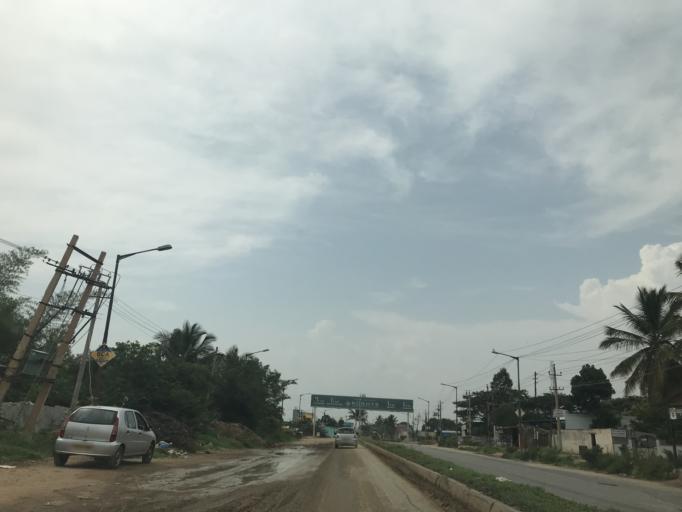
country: IN
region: Karnataka
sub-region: Bangalore Urban
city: Yelahanka
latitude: 13.0886
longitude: 77.6548
